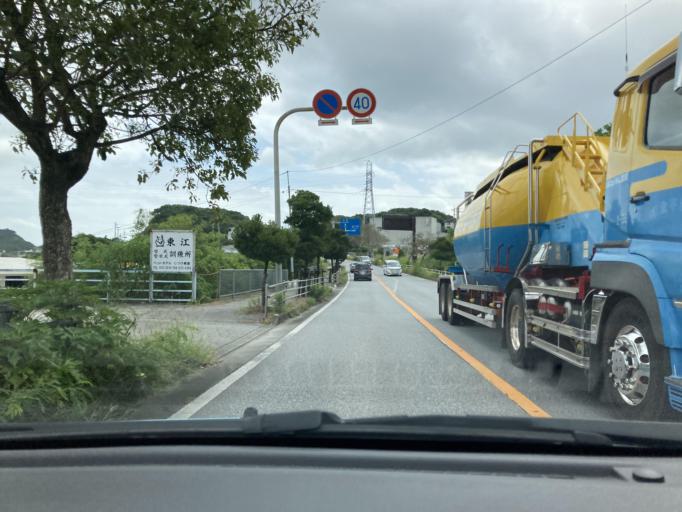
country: JP
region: Okinawa
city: Chatan
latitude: 26.2916
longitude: 127.7848
